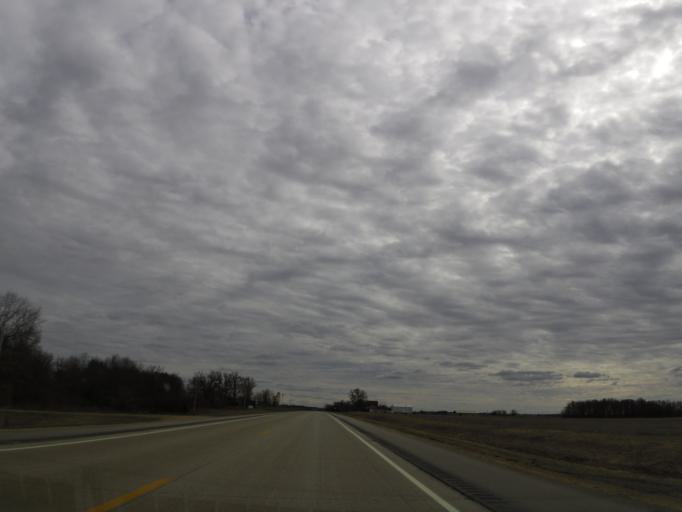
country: US
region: Minnesota
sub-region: Fillmore County
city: Spring Valley
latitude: 43.5191
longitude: -92.3695
